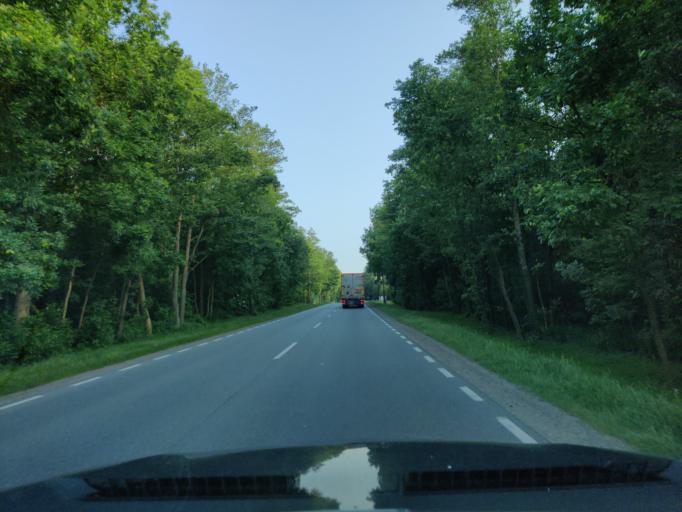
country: PL
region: Masovian Voivodeship
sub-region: Powiat minski
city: Stanislawow
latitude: 52.2797
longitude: 21.5495
